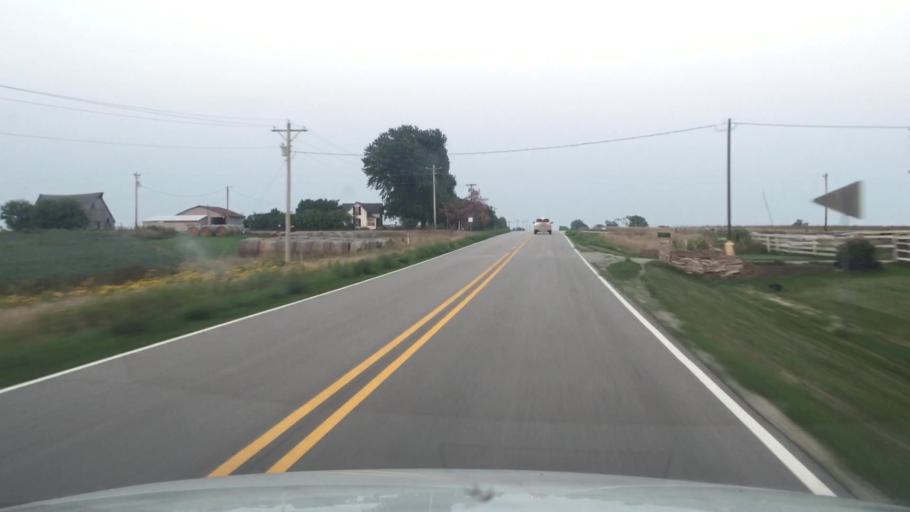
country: US
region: Iowa
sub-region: Warren County
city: Indianola
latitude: 41.1907
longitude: -93.5789
